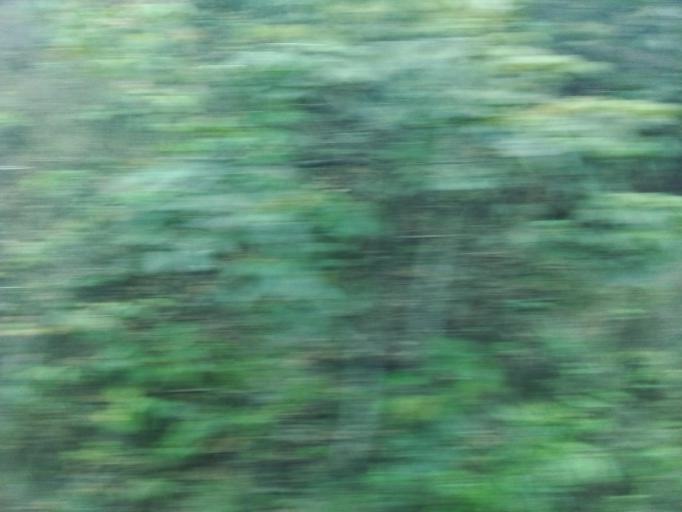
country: BR
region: Minas Gerais
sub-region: Joao Monlevade
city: Joao Monlevade
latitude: -19.8114
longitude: -43.1051
